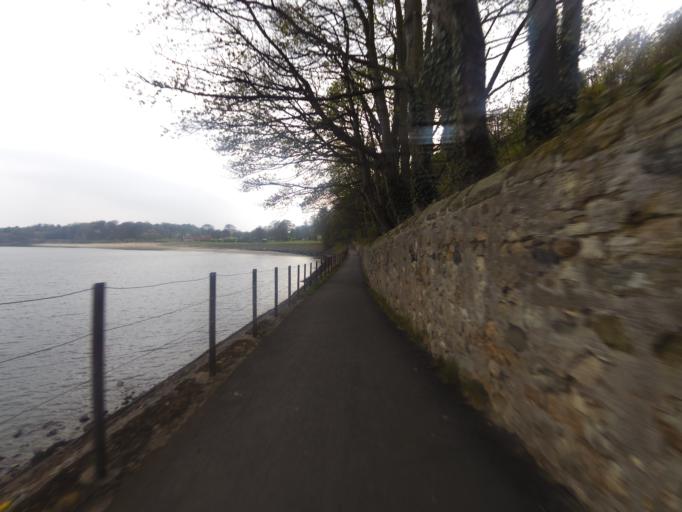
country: GB
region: Scotland
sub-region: Fife
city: Aberdour
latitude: 56.0566
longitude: -3.2816
